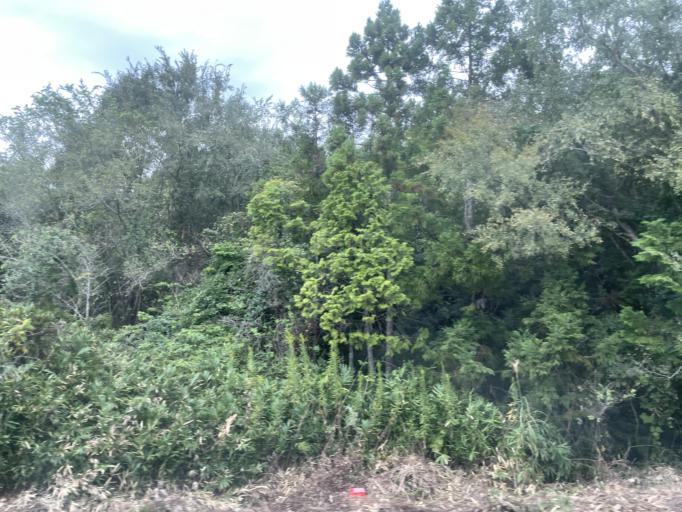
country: JP
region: Wakayama
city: Iwade
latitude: 34.2761
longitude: 135.2599
